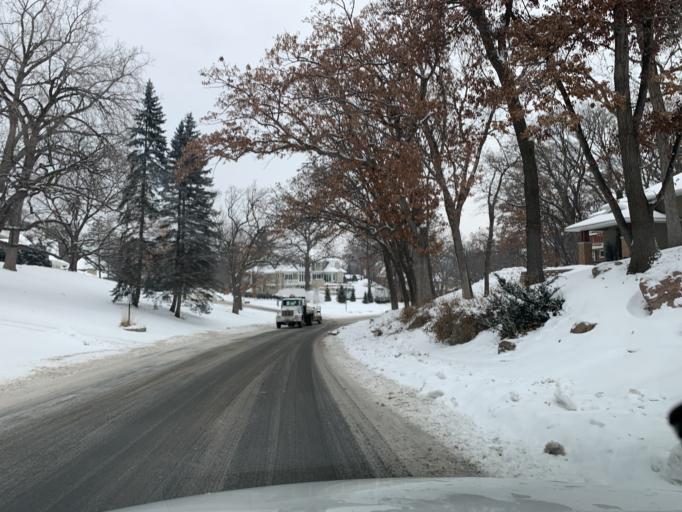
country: US
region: Minnesota
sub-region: Hennepin County
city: Edina
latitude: 44.9123
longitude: -93.3473
